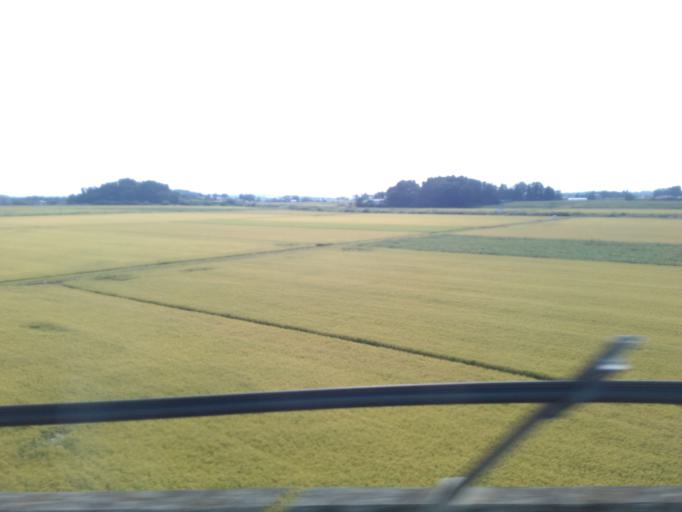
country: JP
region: Iwate
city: Ichinoseki
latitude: 38.7780
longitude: 141.0883
